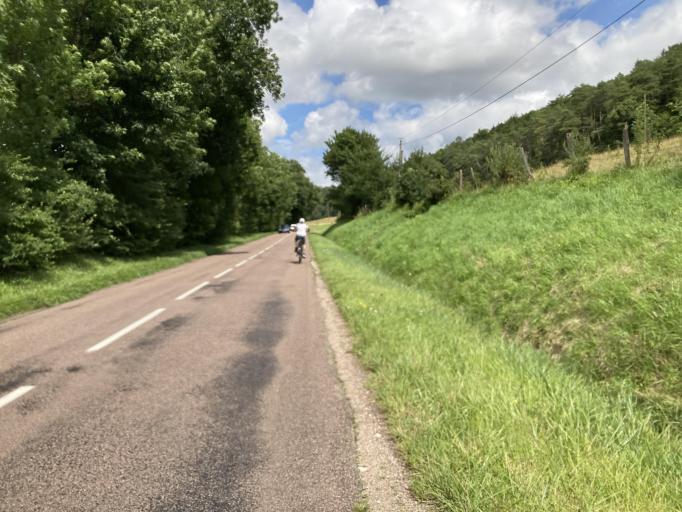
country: FR
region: Bourgogne
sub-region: Departement de la Cote-d'Or
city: Montbard
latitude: 47.6304
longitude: 4.3689
